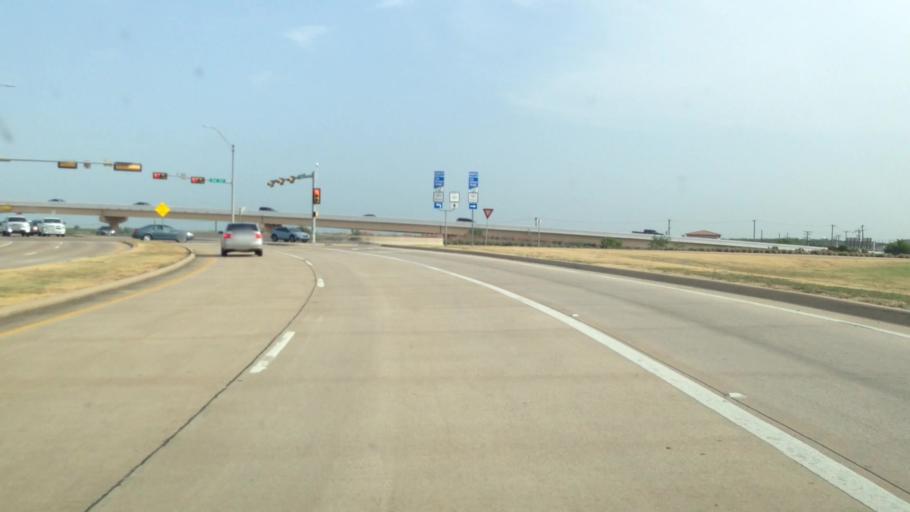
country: US
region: Texas
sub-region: Denton County
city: The Colony
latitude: 33.0499
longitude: -96.9187
